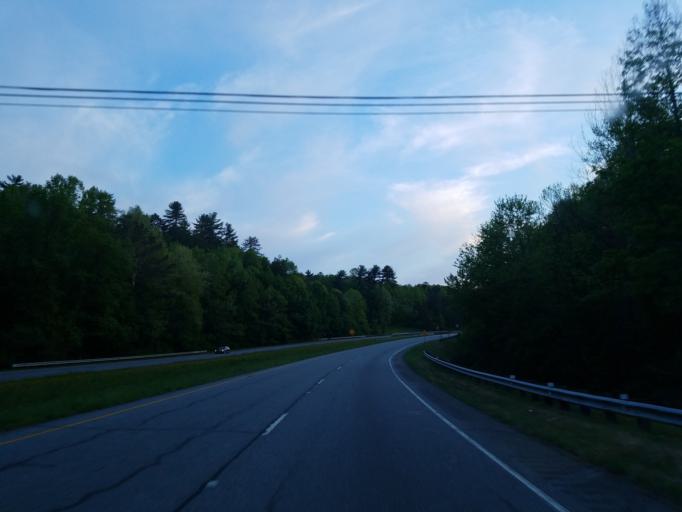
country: US
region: Georgia
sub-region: Gilmer County
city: Ellijay
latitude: 34.7253
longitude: -84.4345
